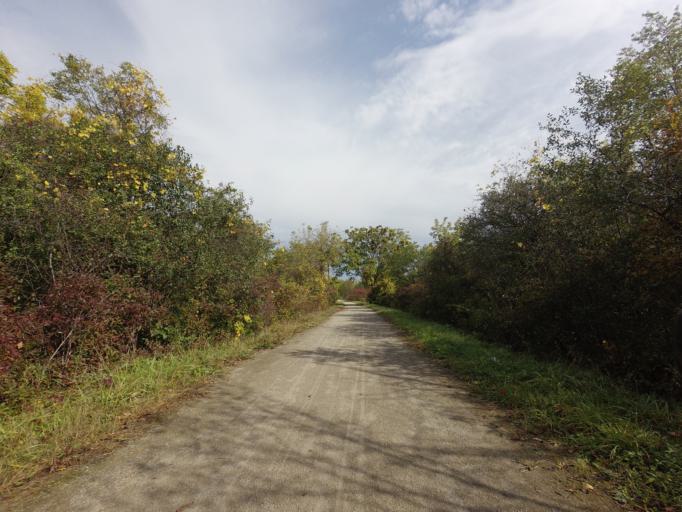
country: CA
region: Ontario
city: Brantford
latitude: 43.1538
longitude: -80.1847
